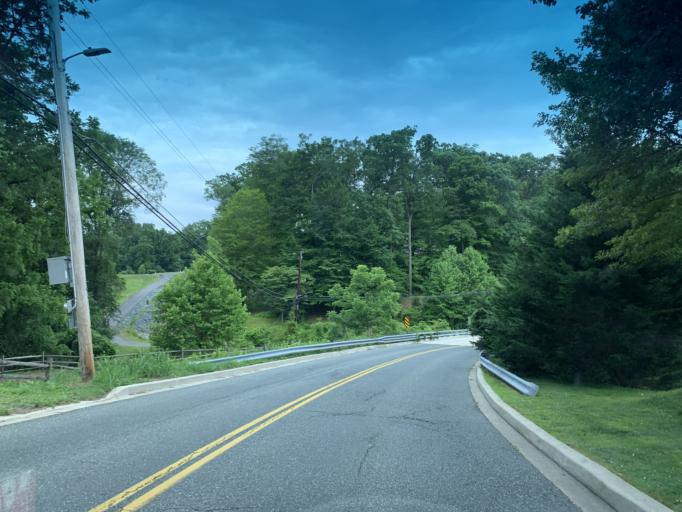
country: US
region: Maryland
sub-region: Harford County
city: Fallston
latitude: 39.5323
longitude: -76.4149
